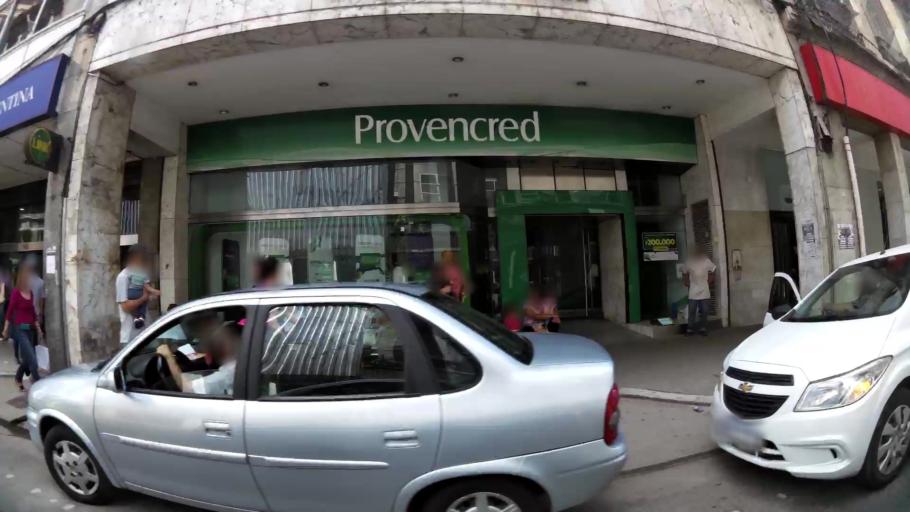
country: AR
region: Santa Fe
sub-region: Departamento de Rosario
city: Rosario
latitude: -32.9446
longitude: -60.6399
